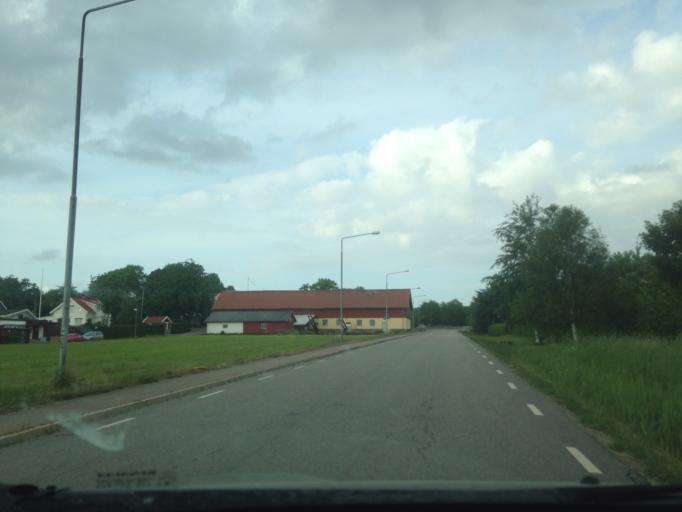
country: SE
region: Vaestra Goetaland
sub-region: Kungalvs Kommun
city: Kungalv
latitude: 57.8022
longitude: 11.9151
